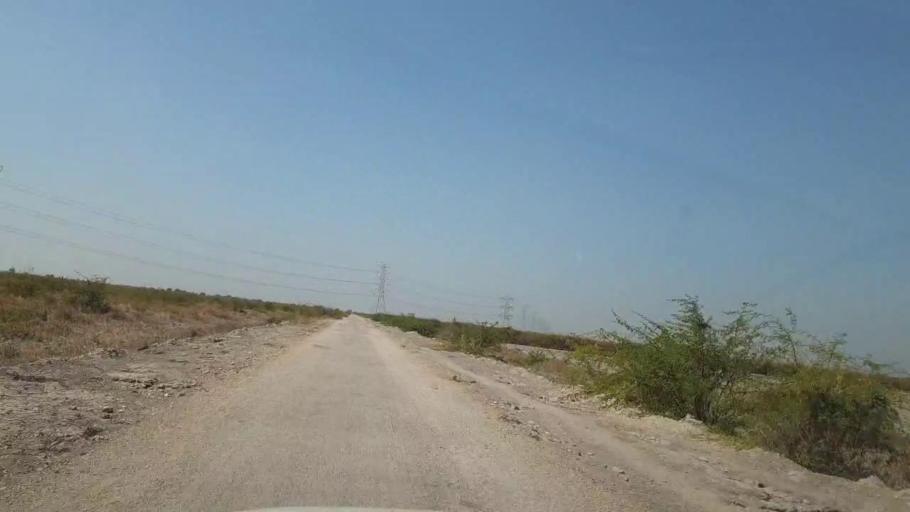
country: PK
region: Sindh
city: Kunri
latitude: 25.0965
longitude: 69.4868
